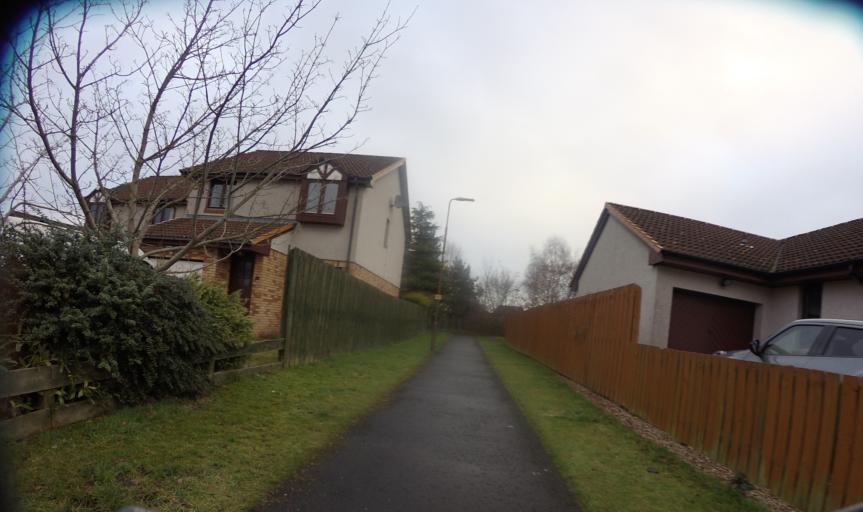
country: GB
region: Scotland
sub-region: West Lothian
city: Livingston
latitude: 55.8645
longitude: -3.5157
